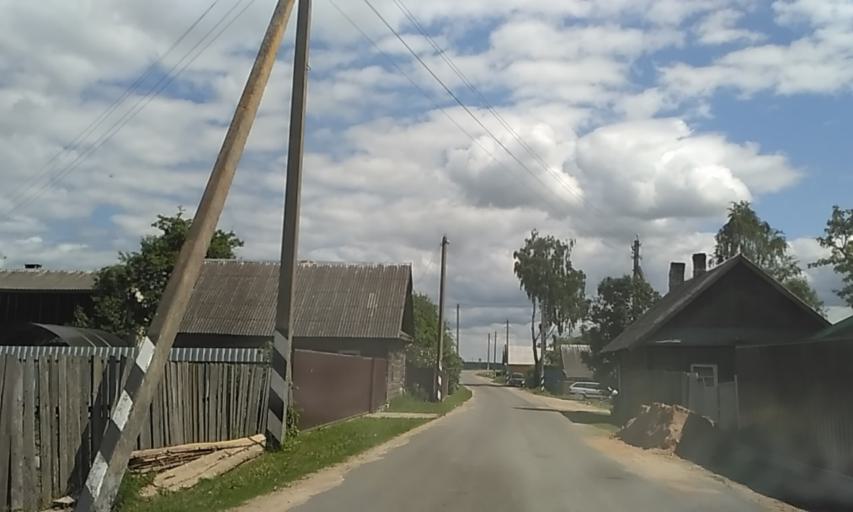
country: BY
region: Minsk
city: Krupki
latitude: 54.3485
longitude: 29.1329
